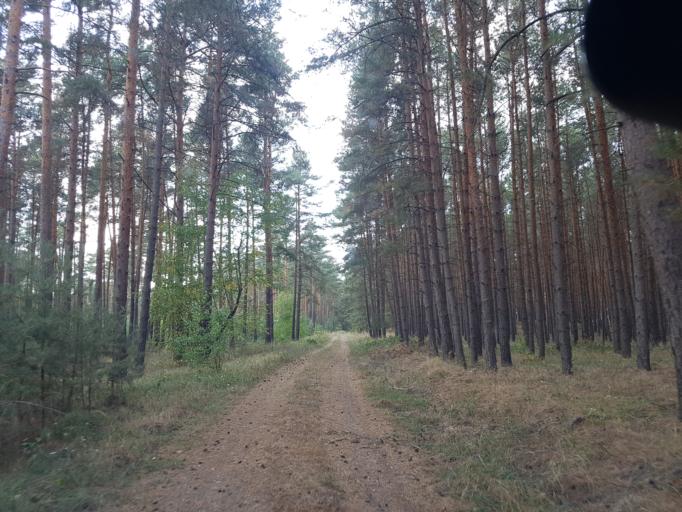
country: DE
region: Brandenburg
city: Treuenbrietzen
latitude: 52.0195
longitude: 12.8759
